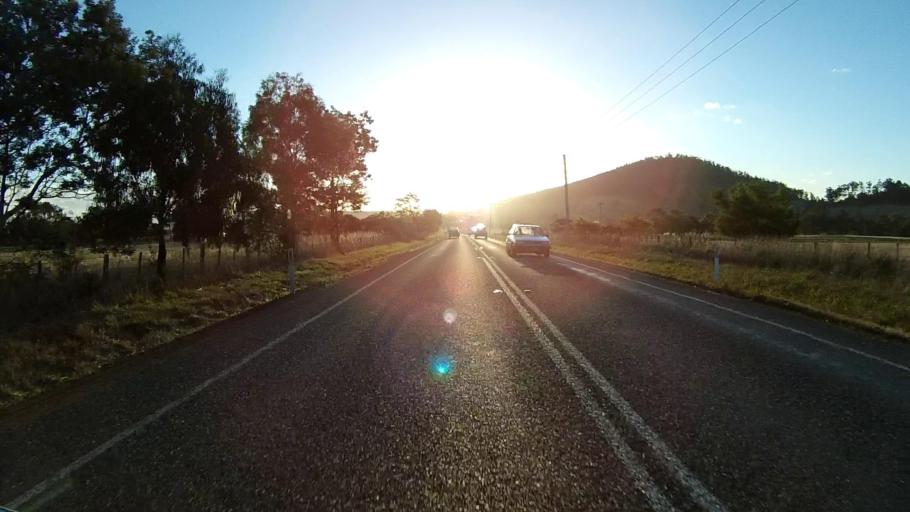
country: AU
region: Tasmania
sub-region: Sorell
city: Sorell
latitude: -42.8040
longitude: 147.6274
